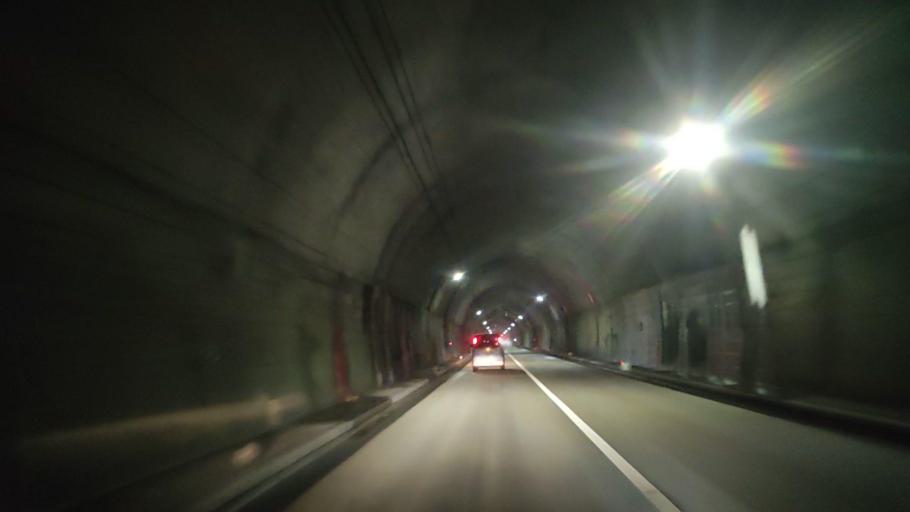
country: JP
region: Gifu
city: Takayama
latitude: 36.1815
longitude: 137.5242
